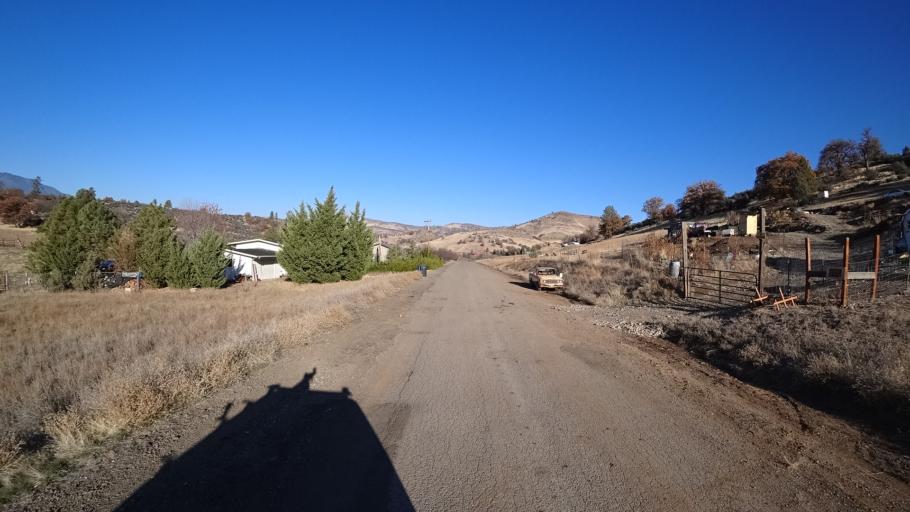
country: US
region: California
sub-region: Siskiyou County
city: Montague
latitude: 41.8934
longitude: -122.4932
